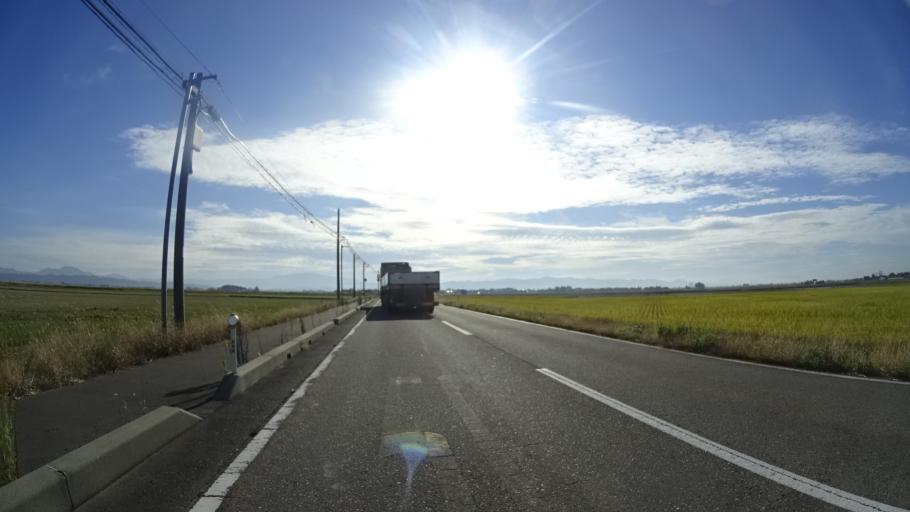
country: JP
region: Niigata
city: Mitsuke
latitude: 37.5677
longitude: 138.8446
